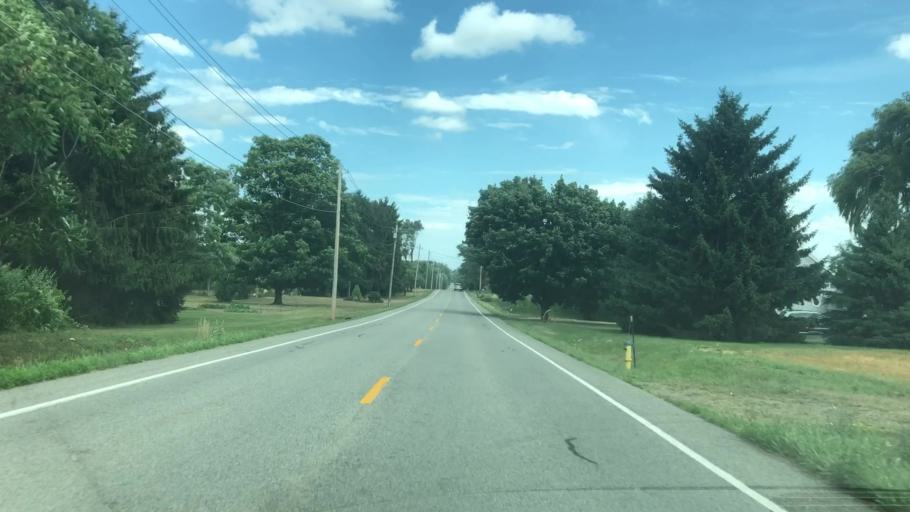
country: US
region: New York
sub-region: Wayne County
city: Macedon
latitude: 43.1076
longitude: -77.3523
